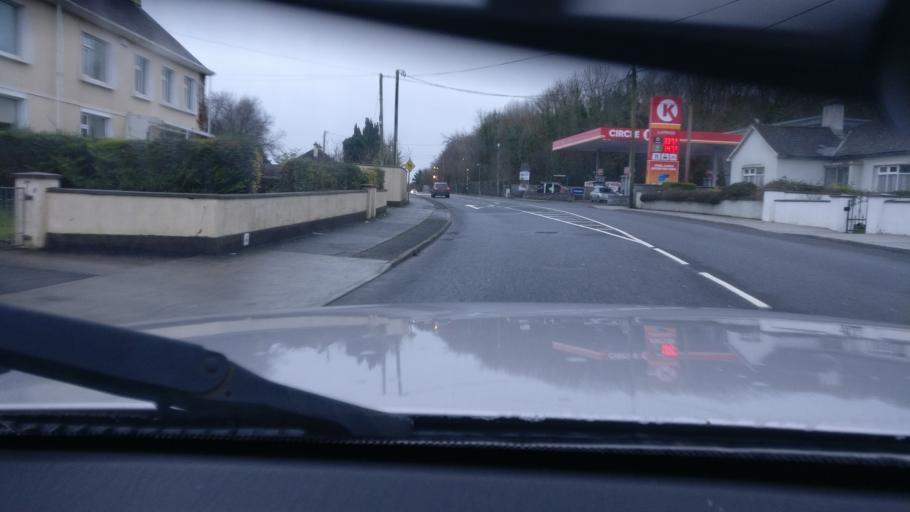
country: IE
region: Connaught
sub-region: County Galway
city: Ballinasloe
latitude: 53.3234
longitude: -8.2400
